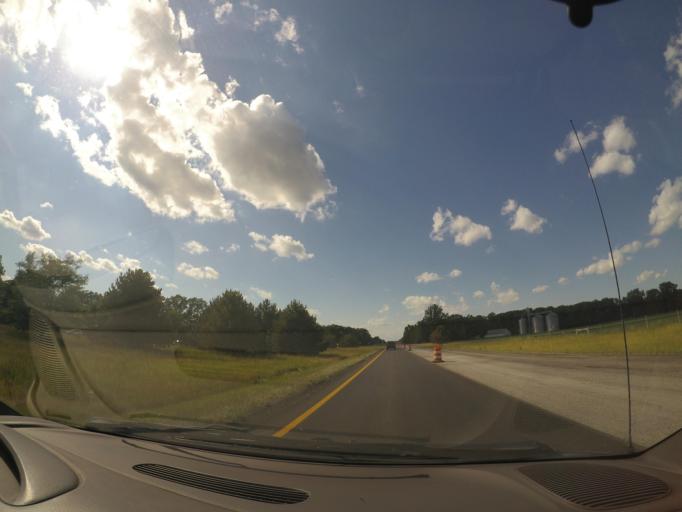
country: US
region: Ohio
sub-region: Sandusky County
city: Fremont
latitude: 41.3363
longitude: -83.0618
